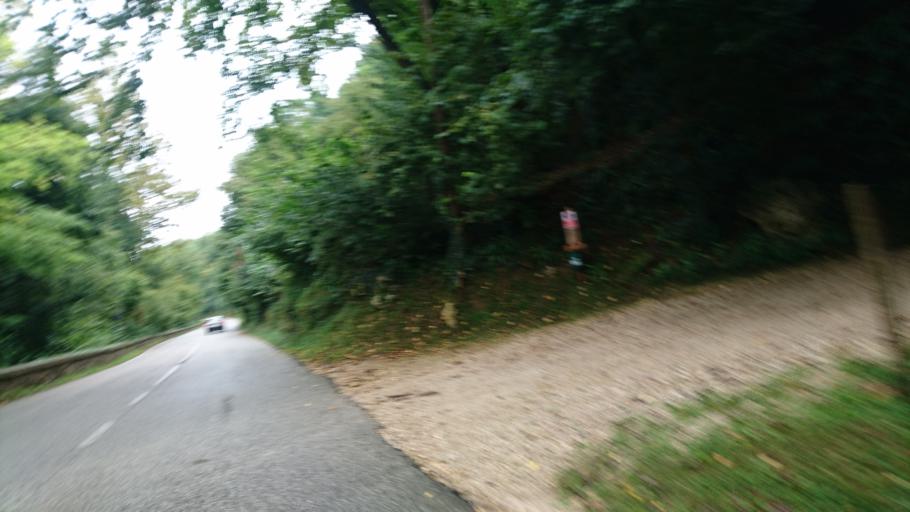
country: IT
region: Veneto
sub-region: Provincia di Treviso
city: Asolo
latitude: 45.7986
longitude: 11.9207
